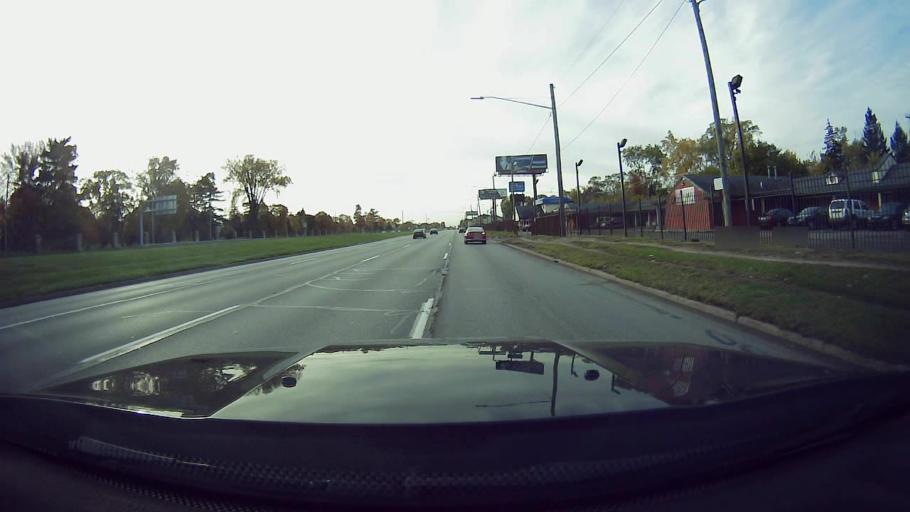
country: US
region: Michigan
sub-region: Wayne County
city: Redford
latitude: 42.4215
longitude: -83.2777
